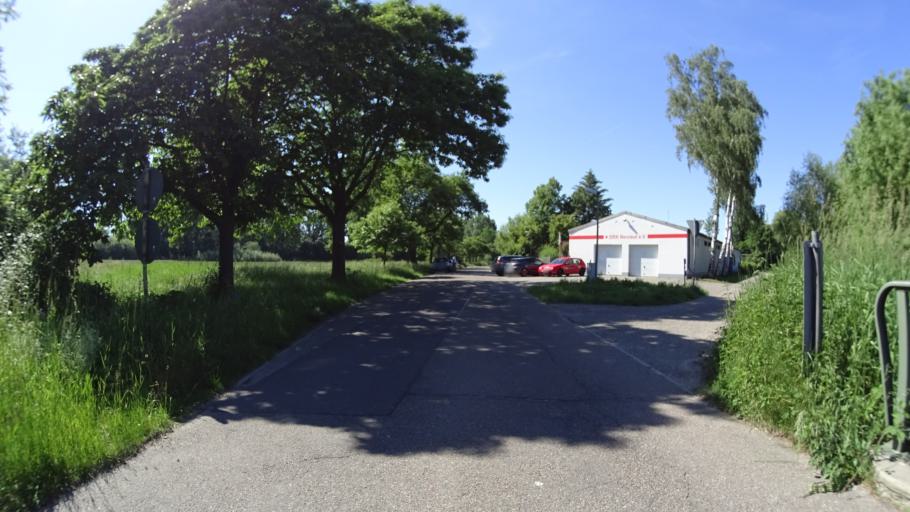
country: DE
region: Baden-Wuerttemberg
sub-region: Karlsruhe Region
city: Eggenstein-Leopoldshafen
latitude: 49.0515
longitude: 8.3725
